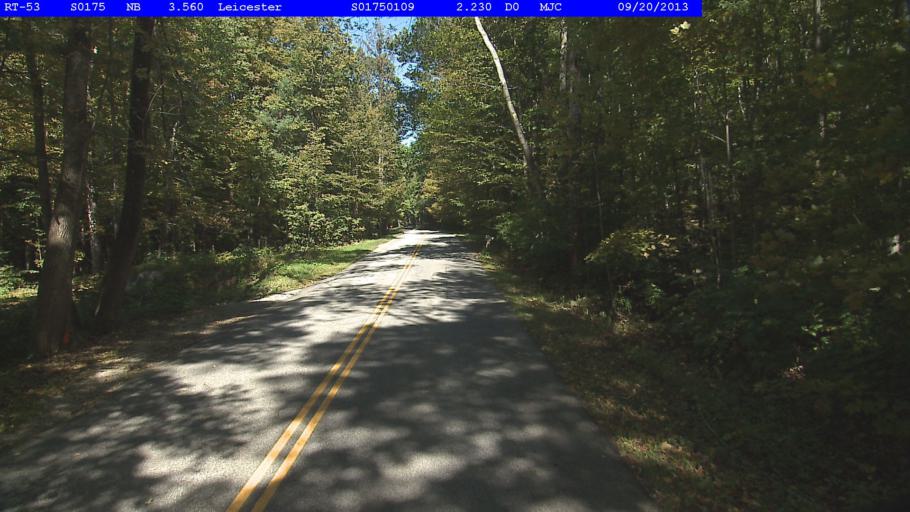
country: US
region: Vermont
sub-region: Rutland County
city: Brandon
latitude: 43.8749
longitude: -73.0637
